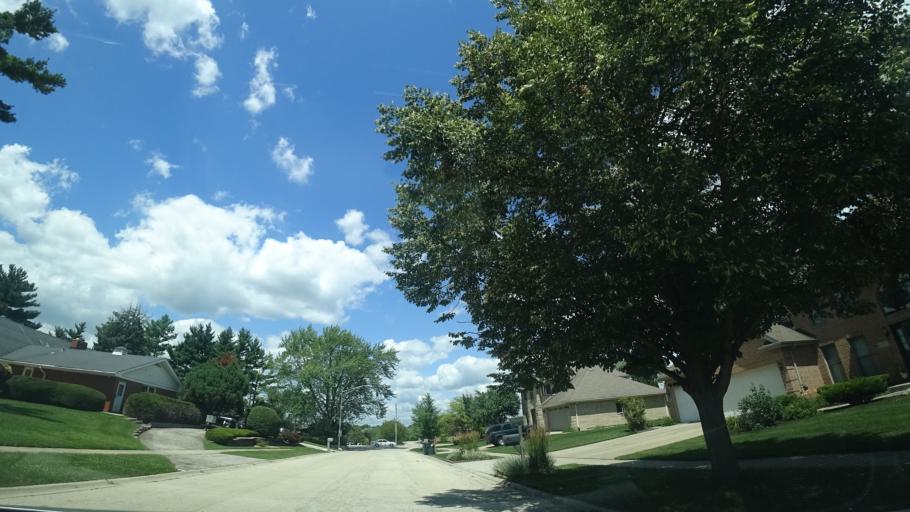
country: US
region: Illinois
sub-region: Cook County
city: Orland Hills
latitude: 41.5853
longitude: -87.8885
